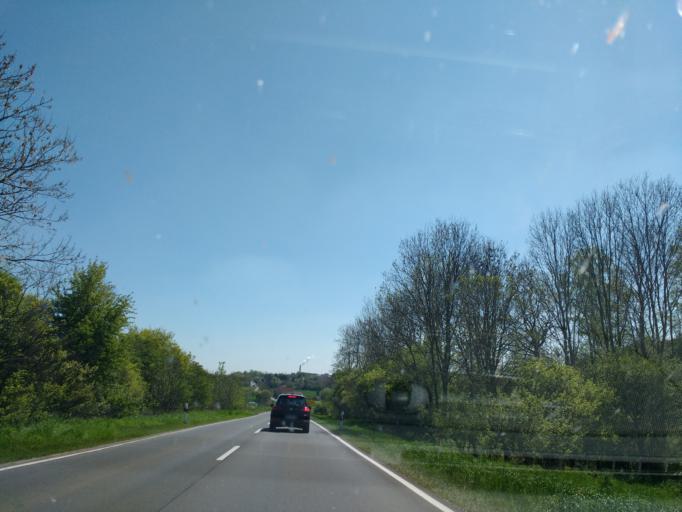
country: DE
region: Saxony-Anhalt
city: Teuchern
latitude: 51.1349
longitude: 12.0515
